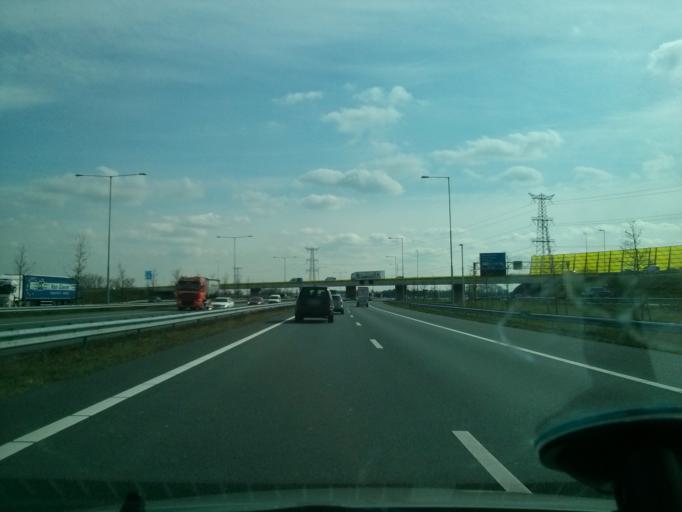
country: NL
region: North Brabant
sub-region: Gemeente 's-Hertogenbosch
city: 's-Hertogenbosch
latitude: 51.7011
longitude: 5.3513
